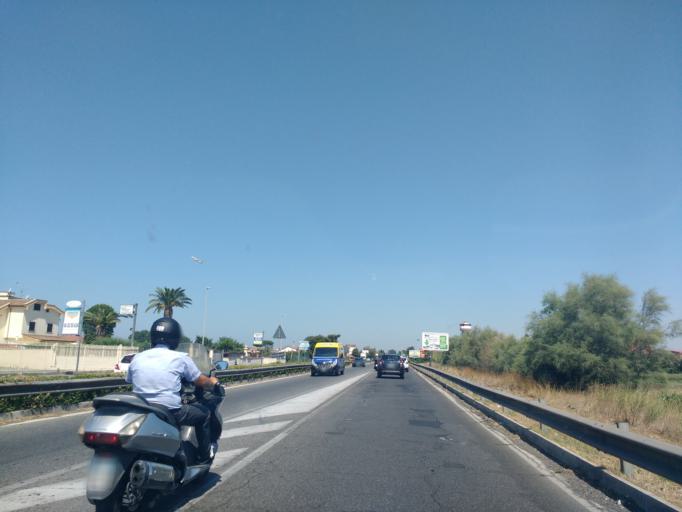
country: IT
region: Latium
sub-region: Citta metropolitana di Roma Capitale
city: Lido di Ostia
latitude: 41.7630
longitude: 12.2665
